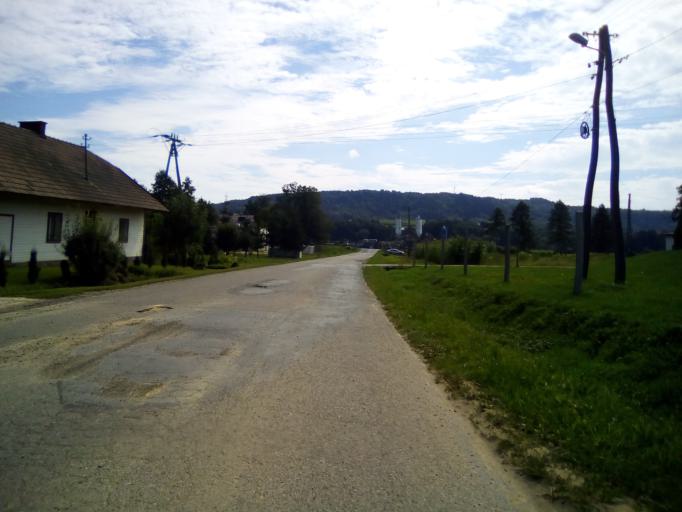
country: PL
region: Subcarpathian Voivodeship
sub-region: Powiat brzozowski
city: Domaradz
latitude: 49.8047
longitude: 21.9271
